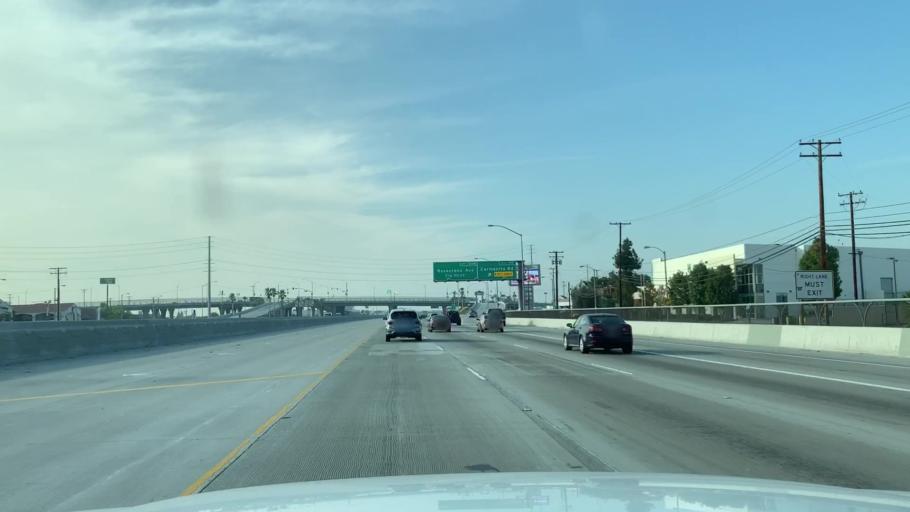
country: US
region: California
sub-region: Los Angeles County
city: La Mirada
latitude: 33.8914
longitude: -118.0423
